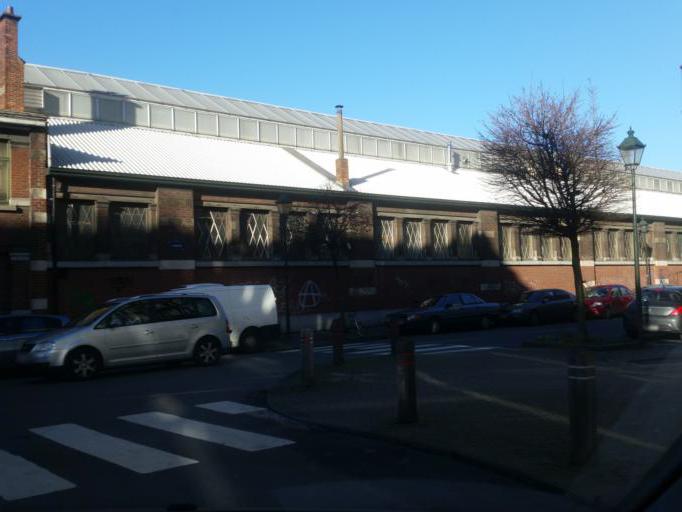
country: BE
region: Brussels Capital
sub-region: Bruxelles-Capitale
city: Brussels
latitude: 50.8293
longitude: 4.3323
